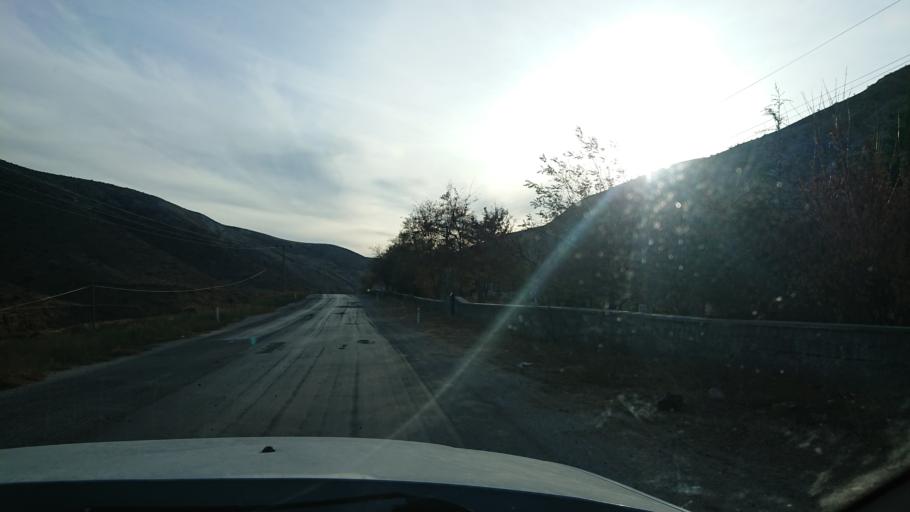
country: TR
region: Ankara
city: Sereflikochisar
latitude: 38.7576
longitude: 33.6954
